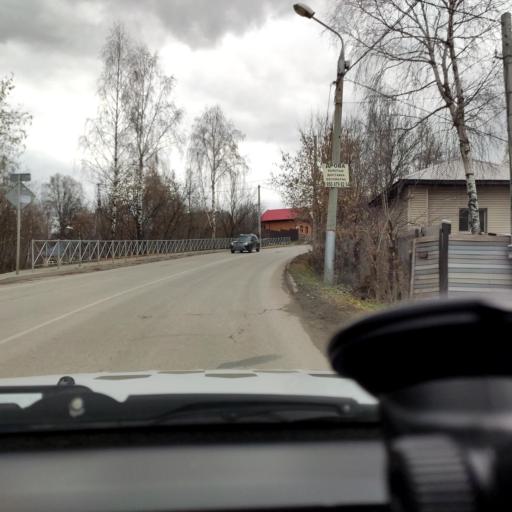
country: RU
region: Perm
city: Perm
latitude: 58.0279
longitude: 56.3148
